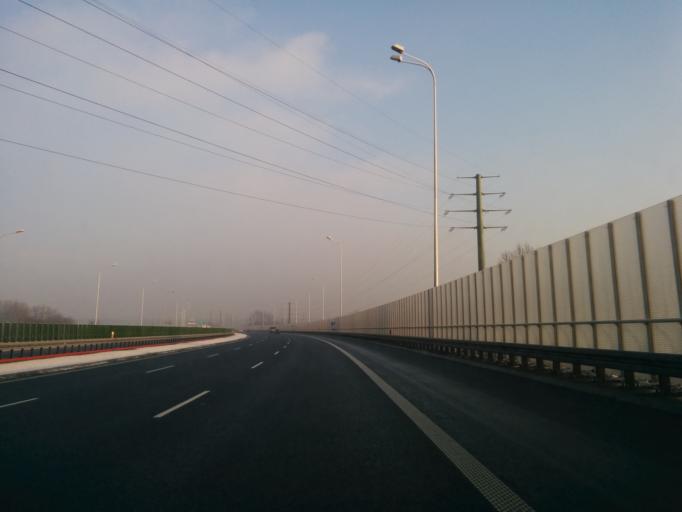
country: PL
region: Silesian Voivodeship
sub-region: Gliwice
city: Gliwice
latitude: 50.3025
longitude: 18.7282
